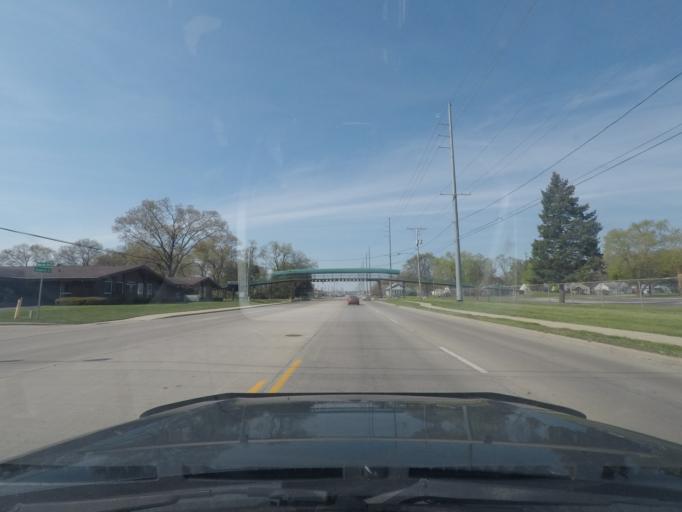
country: US
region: Indiana
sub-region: Elkhart County
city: Elkhart
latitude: 41.6846
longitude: -86.0034
